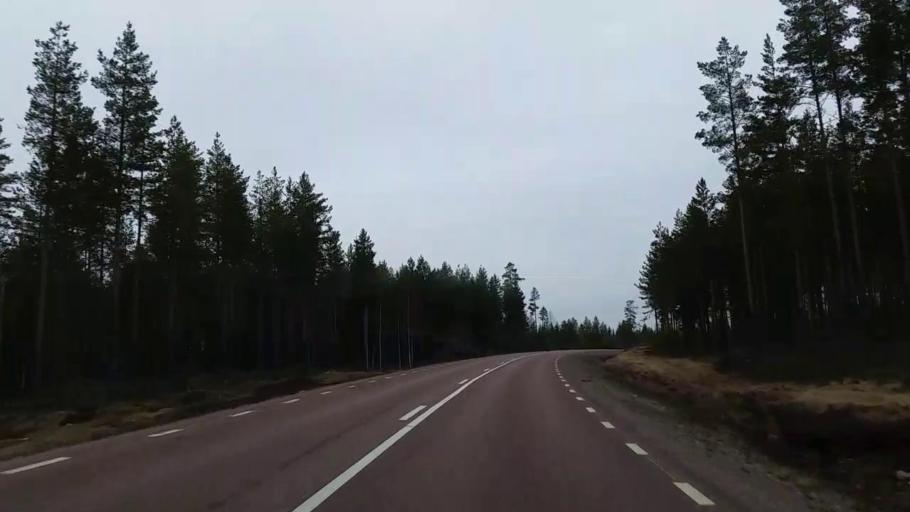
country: SE
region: Gaevleborg
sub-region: Ovanakers Kommun
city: Edsbyn
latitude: 61.2778
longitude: 15.8963
